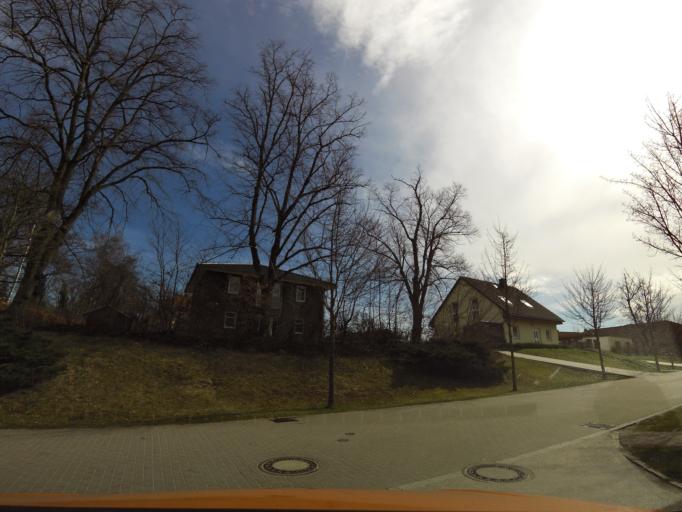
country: DE
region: Brandenburg
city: Belzig
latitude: 52.1456
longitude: 12.5900
